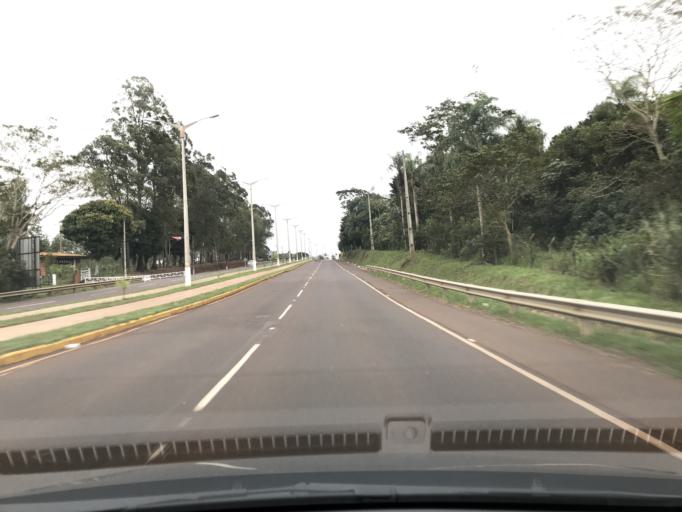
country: PY
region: Canindeyu
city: Salto del Guaira
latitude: -24.0330
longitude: -54.3176
